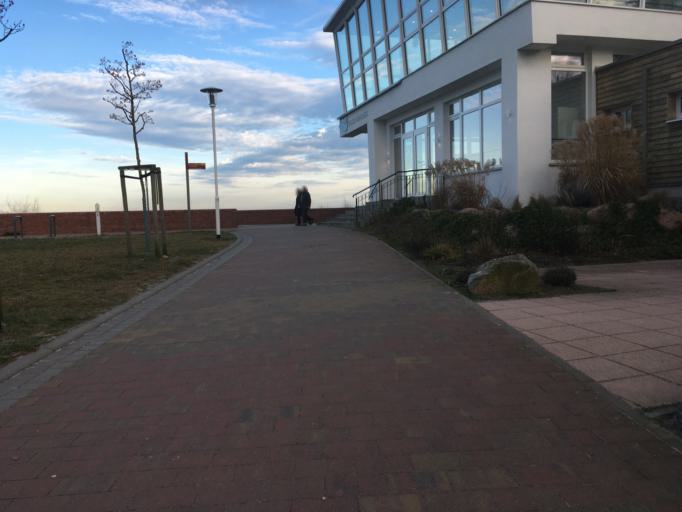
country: DE
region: Mecklenburg-Vorpommern
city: Ostseebad Sellin
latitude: 54.3639
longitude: 13.7135
